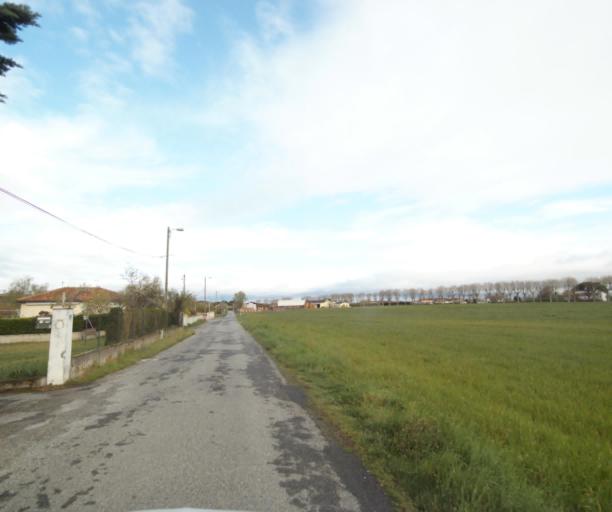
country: FR
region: Midi-Pyrenees
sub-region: Departement de l'Ariege
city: Saverdun
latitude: 43.2294
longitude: 1.5886
